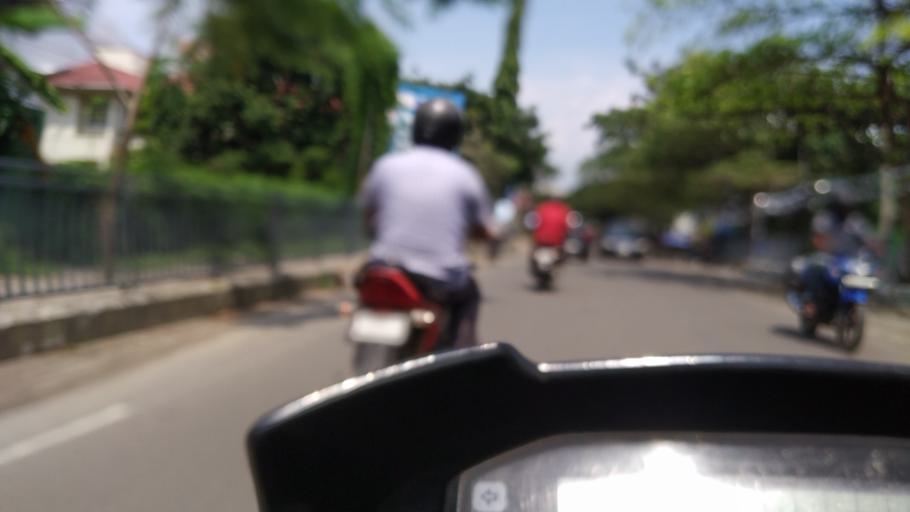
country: IN
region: Kerala
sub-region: Ernakulam
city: Cochin
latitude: 9.9715
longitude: 76.3009
